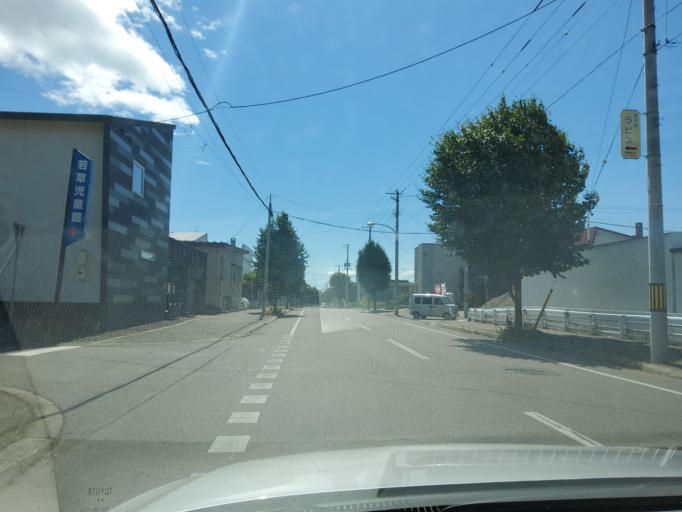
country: JP
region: Hokkaido
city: Obihiro
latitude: 42.9504
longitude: 143.1958
